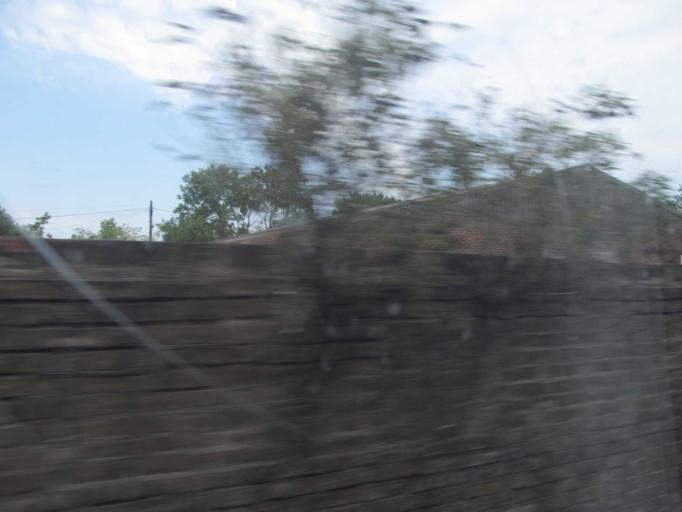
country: GB
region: England
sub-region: Greater London
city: West Drayton
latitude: 51.5086
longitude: -0.4571
